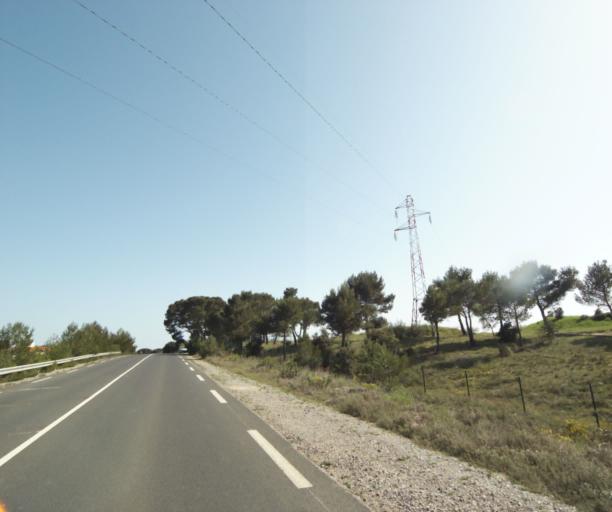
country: FR
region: Languedoc-Roussillon
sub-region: Departement de l'Herault
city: Juvignac
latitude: 43.6229
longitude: 3.7854
